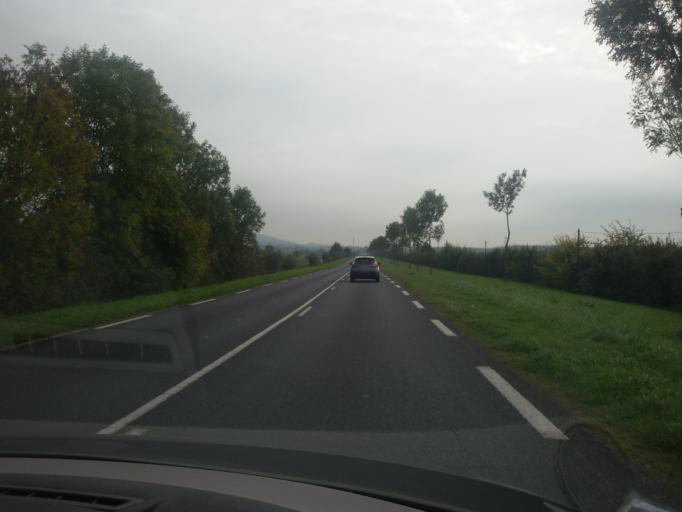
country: FR
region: Lower Normandy
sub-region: Departement du Calvados
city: Dives-sur-Mer
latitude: 49.2423
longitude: -0.1005
